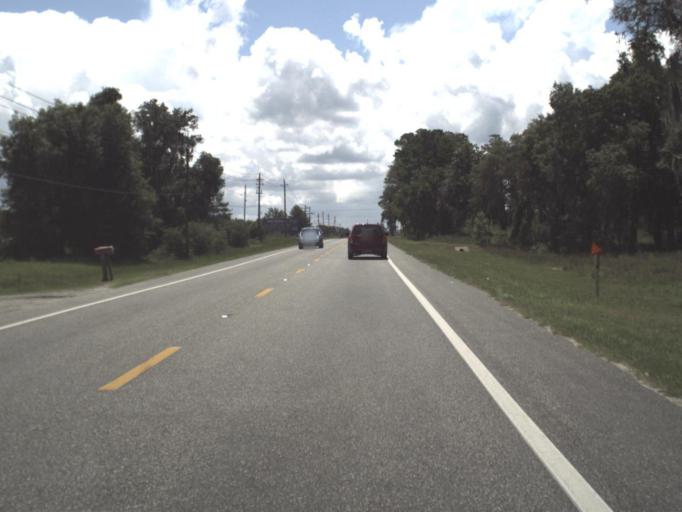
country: US
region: Florida
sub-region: Putnam County
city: Crescent City
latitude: 29.4861
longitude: -81.5688
